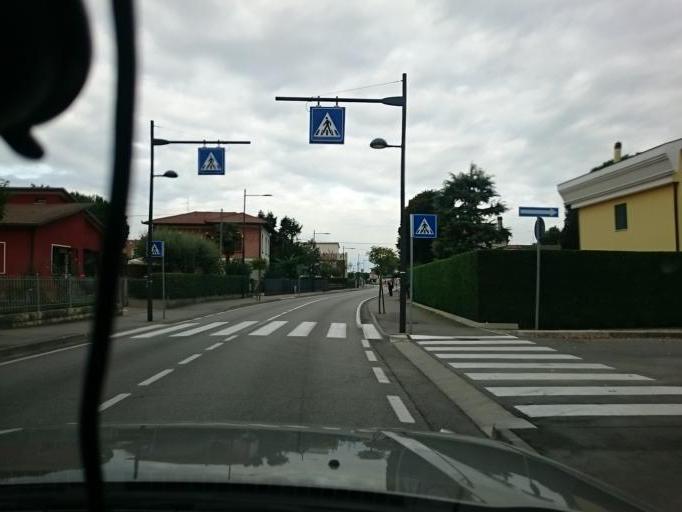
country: IT
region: Veneto
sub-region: Provincia di Padova
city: Saccolongo
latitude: 45.4044
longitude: 11.7450
